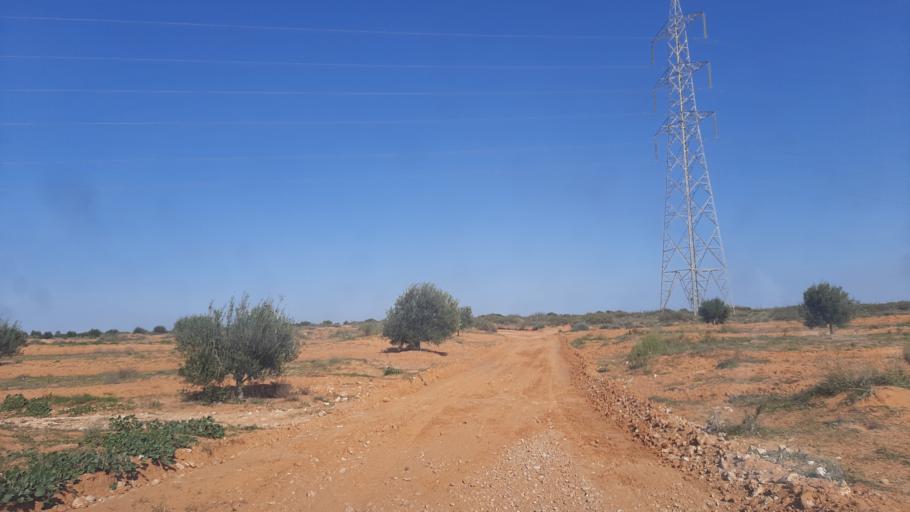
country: TN
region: Madanin
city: Medenine
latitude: 33.2787
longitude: 10.7750
